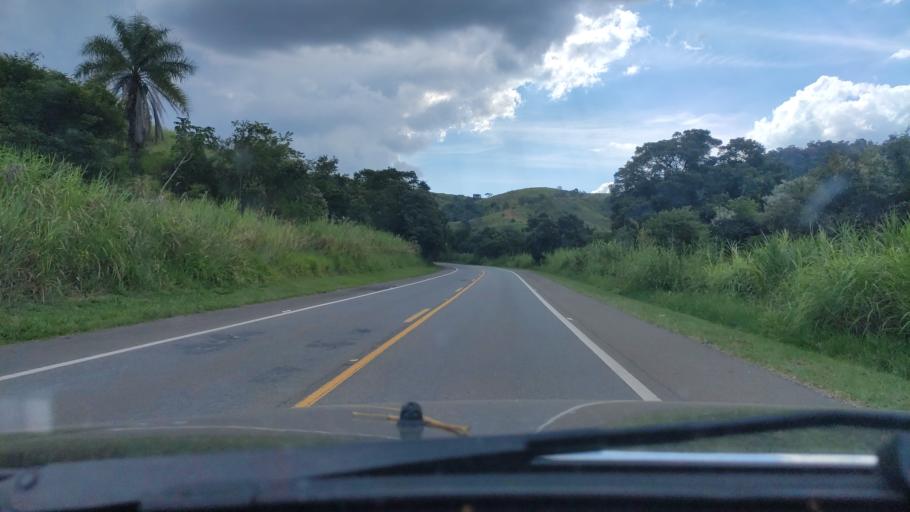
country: BR
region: Sao Paulo
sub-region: Aguas De Lindoia
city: Aguas de Lindoia
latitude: -22.4698
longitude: -46.7006
